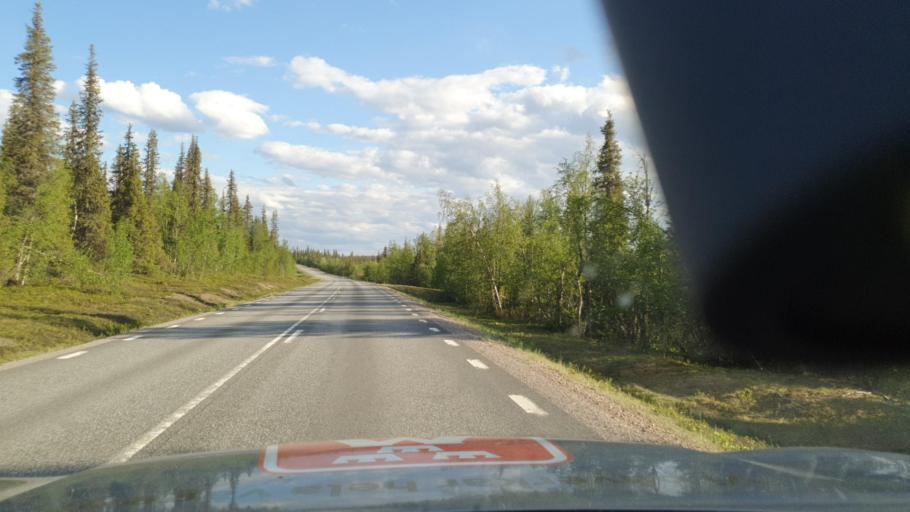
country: SE
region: Norrbotten
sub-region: Gallivare Kommun
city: Malmberget
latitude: 67.3163
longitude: 21.0812
